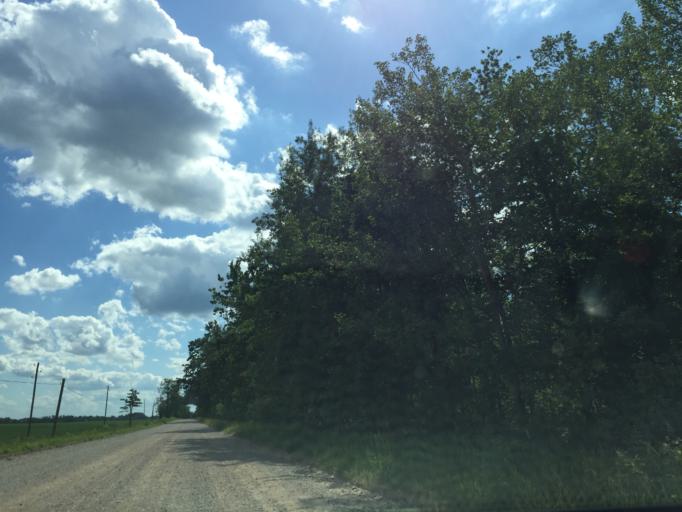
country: LV
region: Engure
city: Smarde
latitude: 56.8628
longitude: 23.3208
